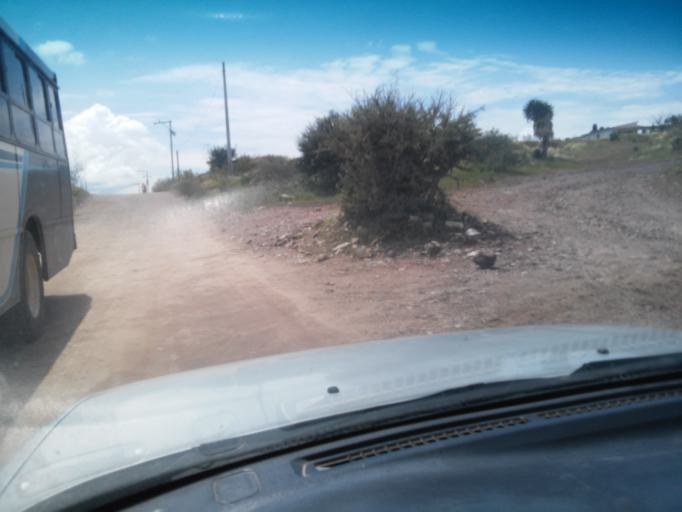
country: MX
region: Durango
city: Victoria de Durango
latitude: 23.9897
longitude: -104.7110
